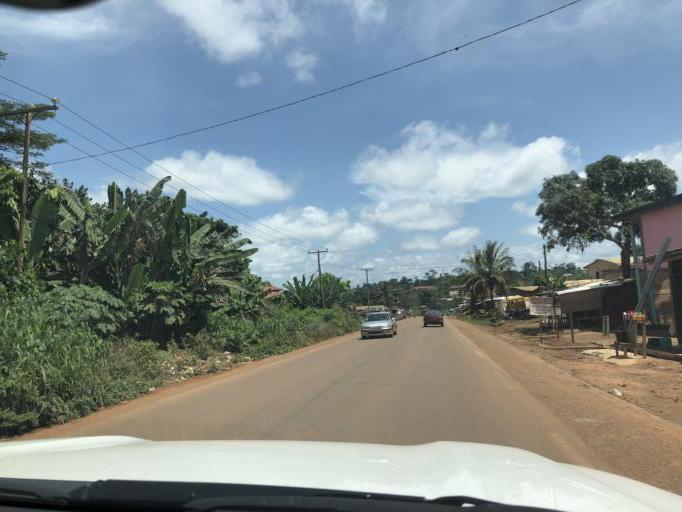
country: CM
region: Centre
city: Yaounde
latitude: 3.8646
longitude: 11.6132
